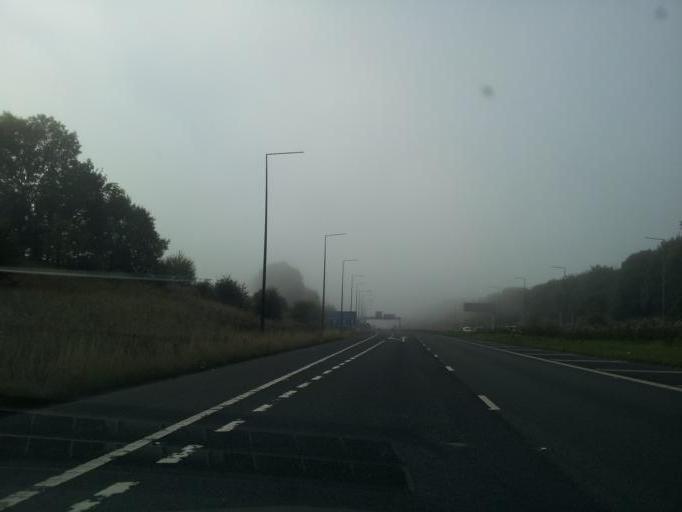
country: GB
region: England
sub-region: Borough of Rochdale
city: Rochdale
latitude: 53.5822
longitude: -2.1581
